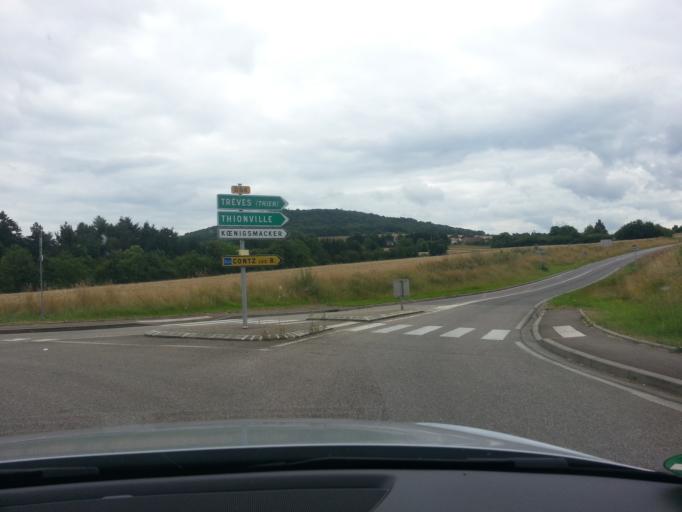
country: FR
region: Lorraine
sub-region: Departement de la Moselle
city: Sierck-les-Bains
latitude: 49.4467
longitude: 6.3438
